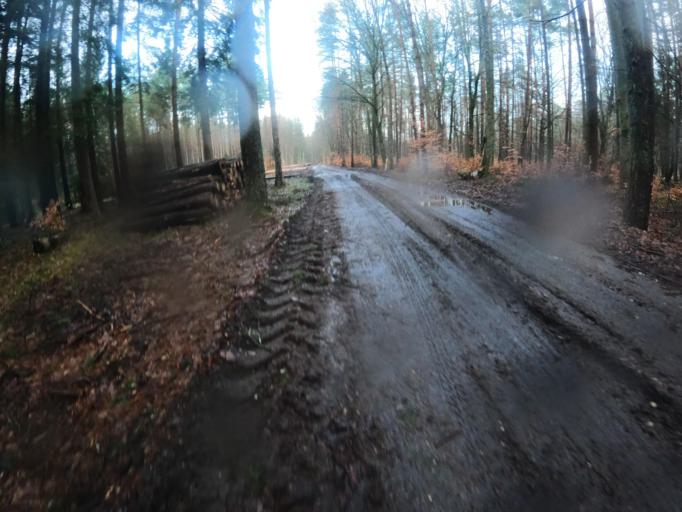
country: PL
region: West Pomeranian Voivodeship
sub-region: Powiat slawienski
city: Slawno
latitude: 54.2621
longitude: 16.7104
